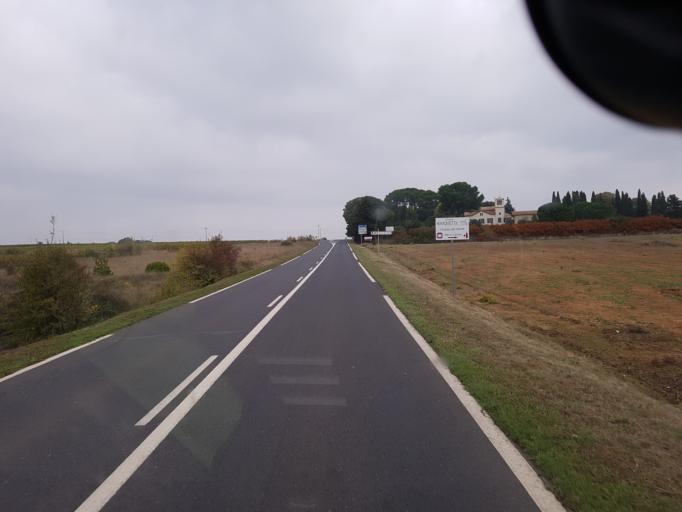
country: FR
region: Languedoc-Roussillon
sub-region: Departement de l'Herault
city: Pinet
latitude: 43.3875
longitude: 3.5369
